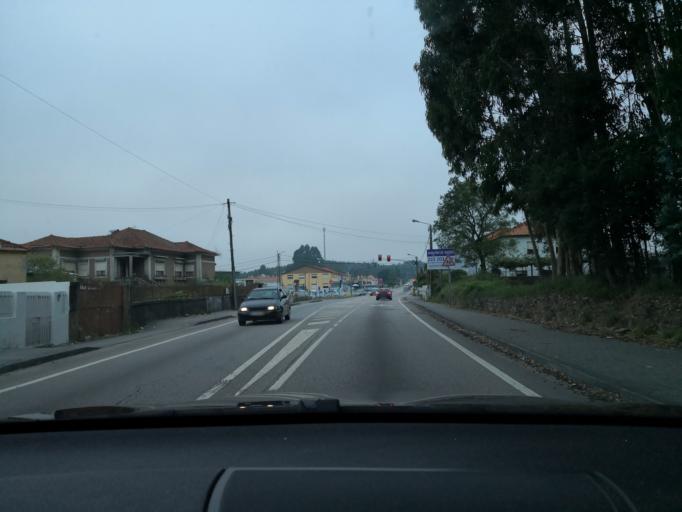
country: PT
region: Aveiro
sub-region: Santa Maria da Feira
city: Argoncilhe
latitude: 41.0120
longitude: -8.5562
